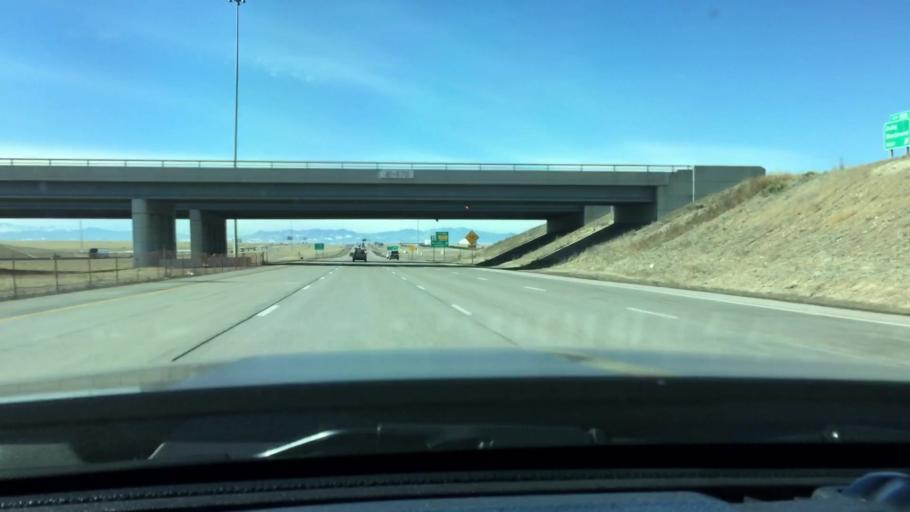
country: US
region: Colorado
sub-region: Adams County
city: Aurora
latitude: 39.8352
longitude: -104.7462
